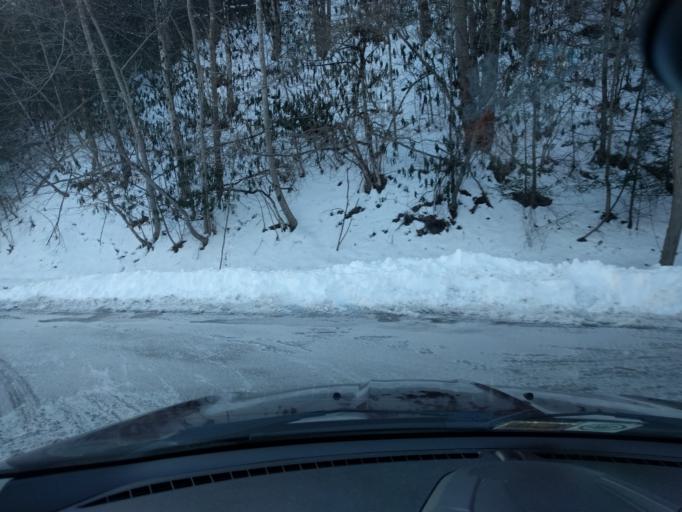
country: US
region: West Virginia
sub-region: Pocahontas County
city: Marlinton
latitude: 38.2186
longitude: -80.0945
